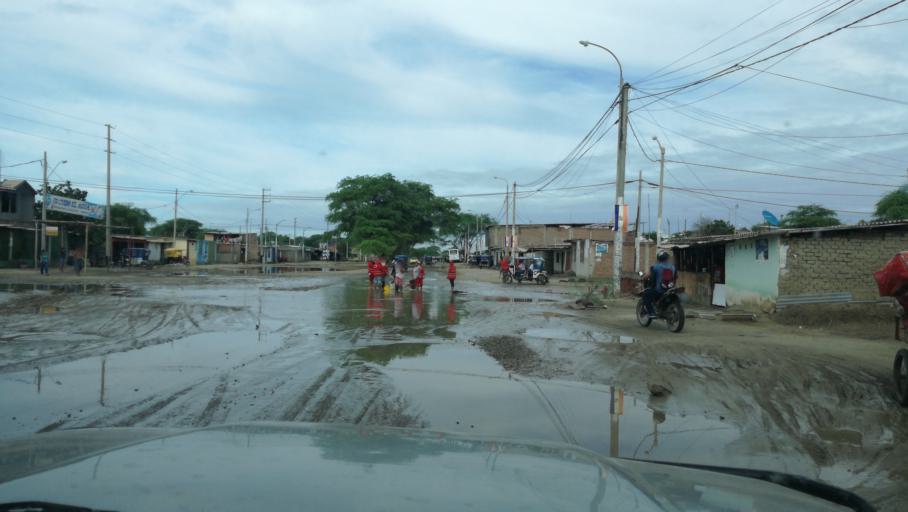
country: PE
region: Piura
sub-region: Provincia de Piura
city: Piura
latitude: -5.1859
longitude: -80.6751
